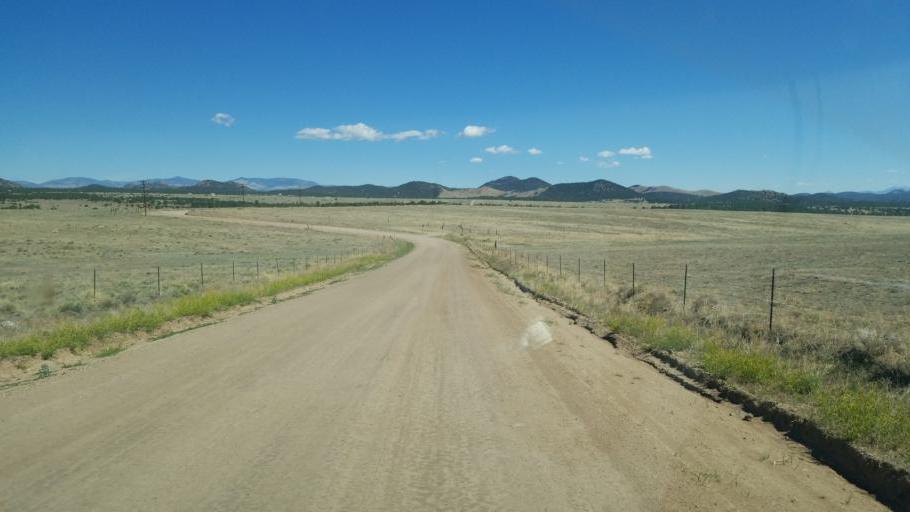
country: US
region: Colorado
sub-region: Custer County
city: Westcliffe
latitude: 38.2607
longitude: -105.4999
